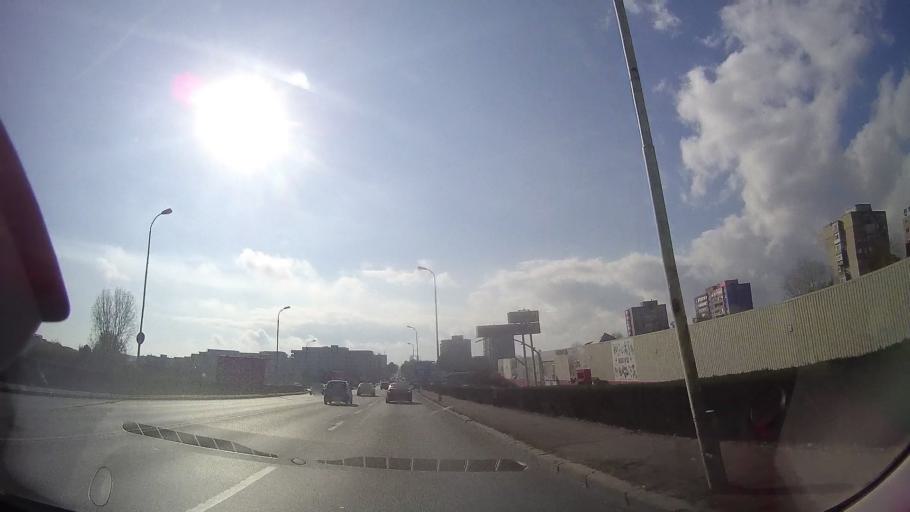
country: RO
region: Constanta
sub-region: Municipiul Constanta
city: Constanta
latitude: 44.1476
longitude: 28.6254
